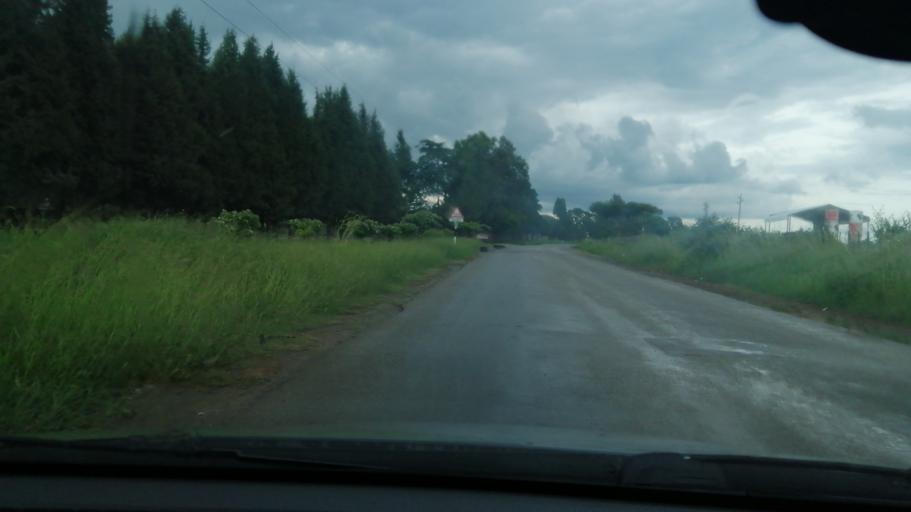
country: ZW
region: Harare
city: Harare
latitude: -17.7372
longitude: 31.0713
